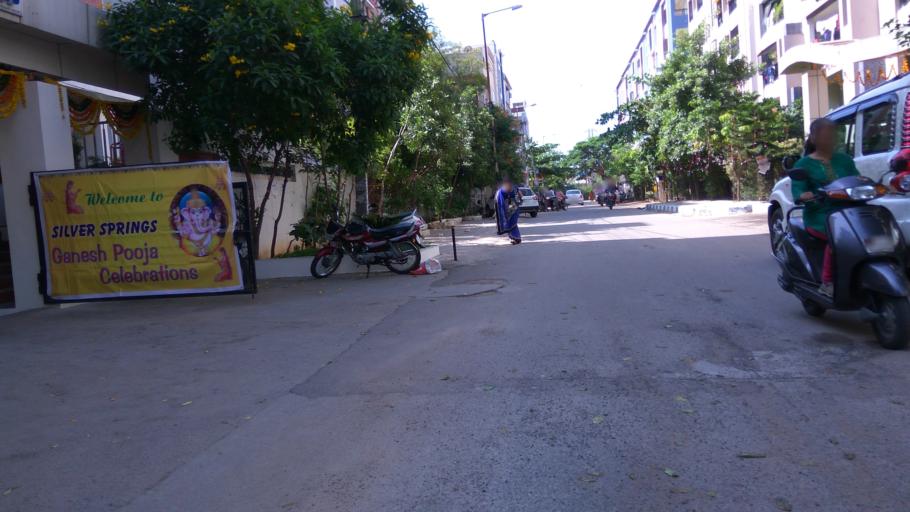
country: IN
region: Telangana
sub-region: Rangareddi
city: Kukatpalli
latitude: 17.4555
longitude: 78.4361
